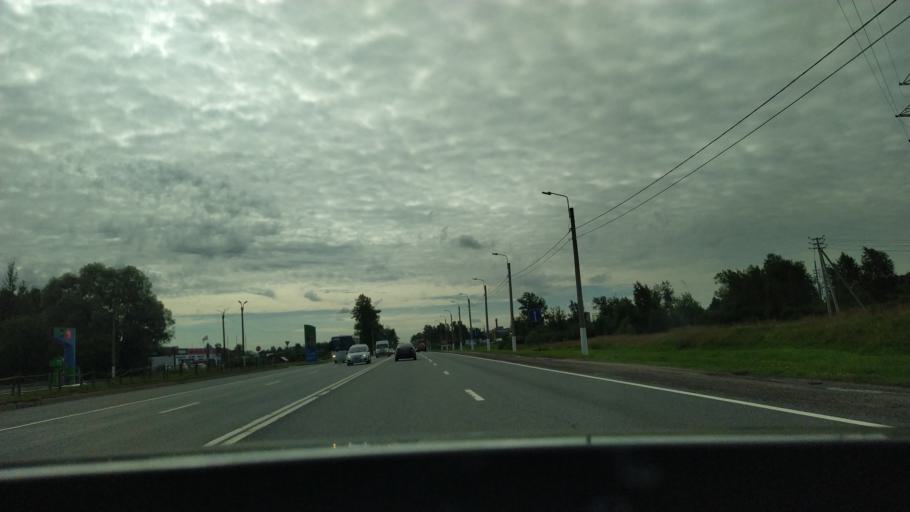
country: RU
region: Leningrad
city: Tosno
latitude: 59.5653
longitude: 30.8325
